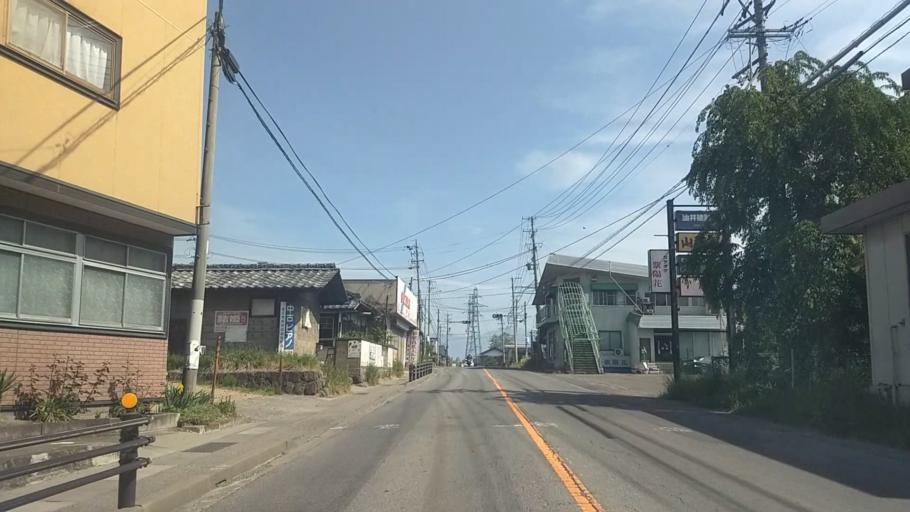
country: JP
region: Nagano
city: Saku
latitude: 36.1832
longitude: 138.4816
